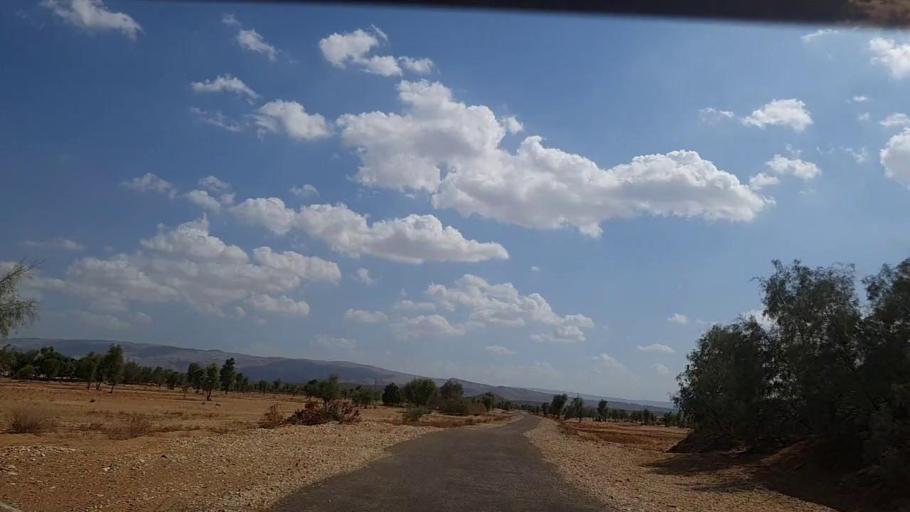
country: PK
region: Sindh
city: Johi
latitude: 26.5105
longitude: 67.4467
